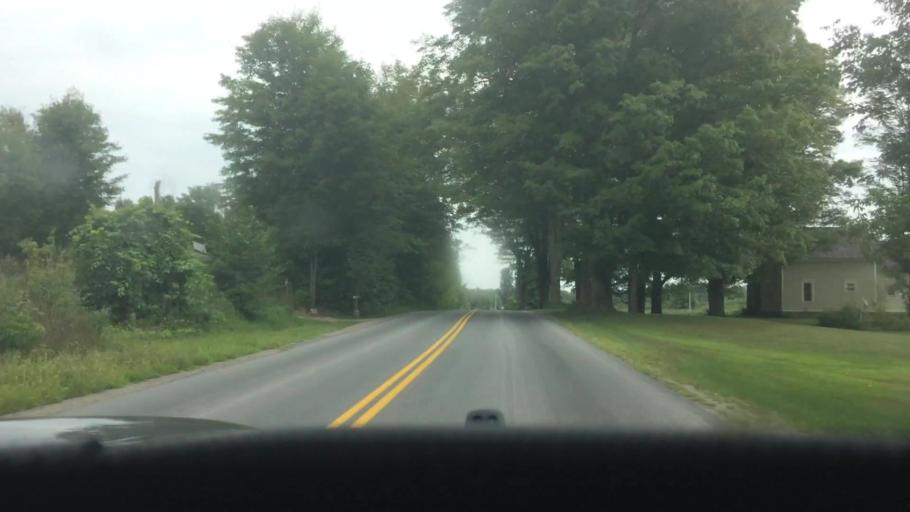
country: US
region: New York
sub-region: St. Lawrence County
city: Canton
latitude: 44.4998
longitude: -75.2934
